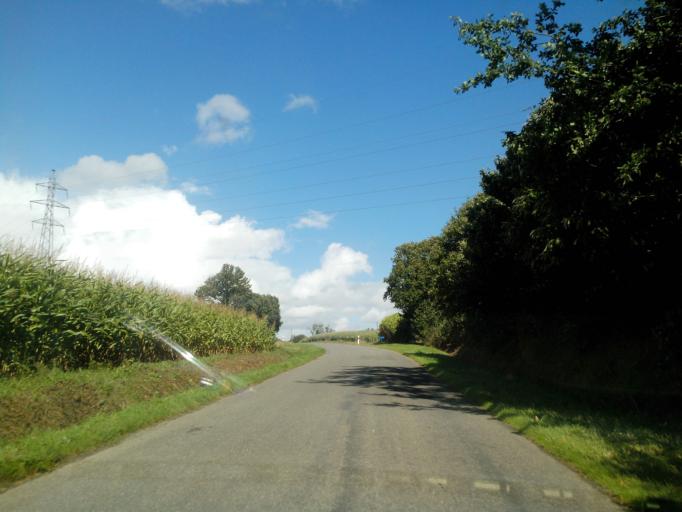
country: FR
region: Brittany
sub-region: Departement des Cotes-d'Armor
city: Merdrignac
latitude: 48.1771
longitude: -2.4156
